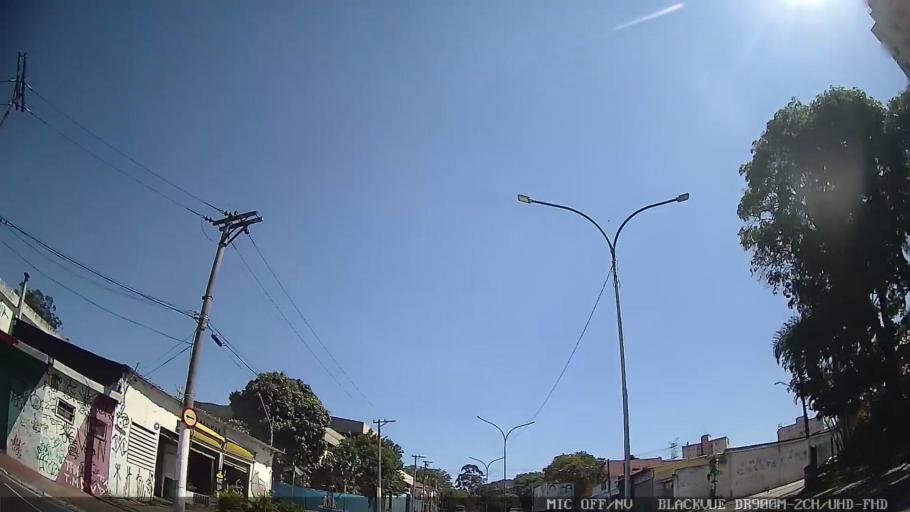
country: BR
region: Sao Paulo
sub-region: Sao Caetano Do Sul
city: Sao Caetano do Sul
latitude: -23.5841
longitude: -46.4988
